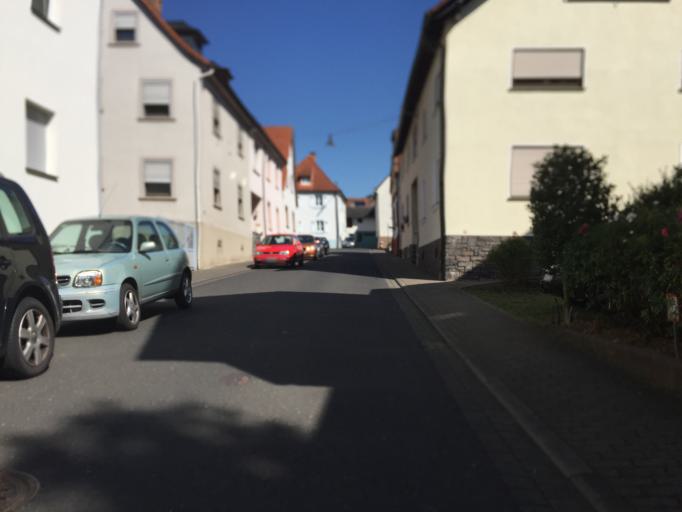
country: DE
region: Bavaria
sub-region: Regierungsbezirk Unterfranken
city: Goldbach
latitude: 50.0001
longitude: 9.1871
